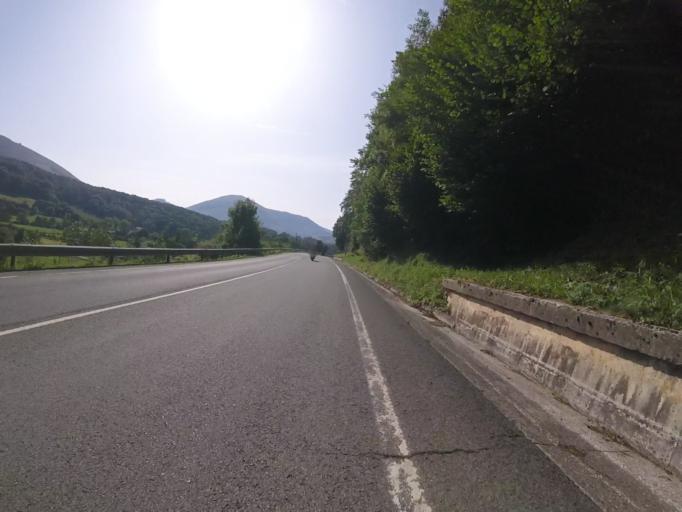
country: ES
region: Navarre
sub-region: Provincia de Navarra
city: Zugarramurdi
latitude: 43.1993
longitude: -1.4846
